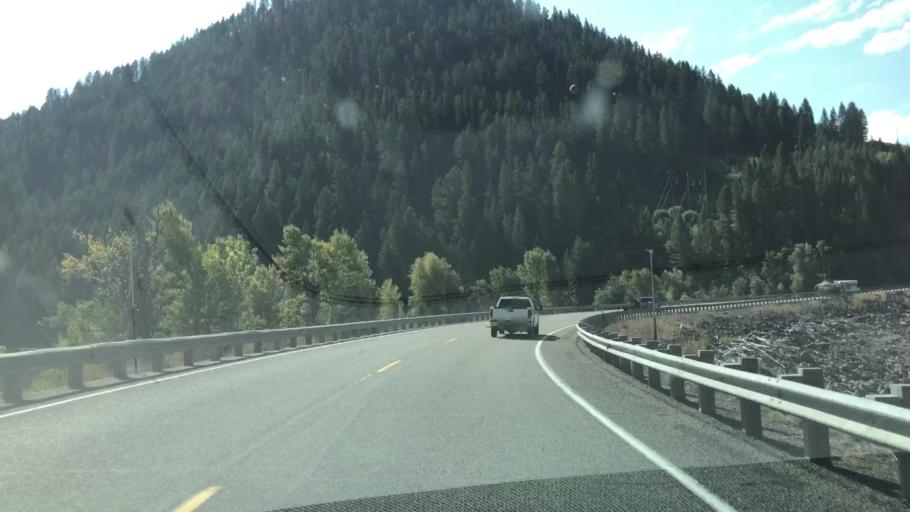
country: US
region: Idaho
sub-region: Teton County
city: Victor
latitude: 43.3191
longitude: -111.1451
